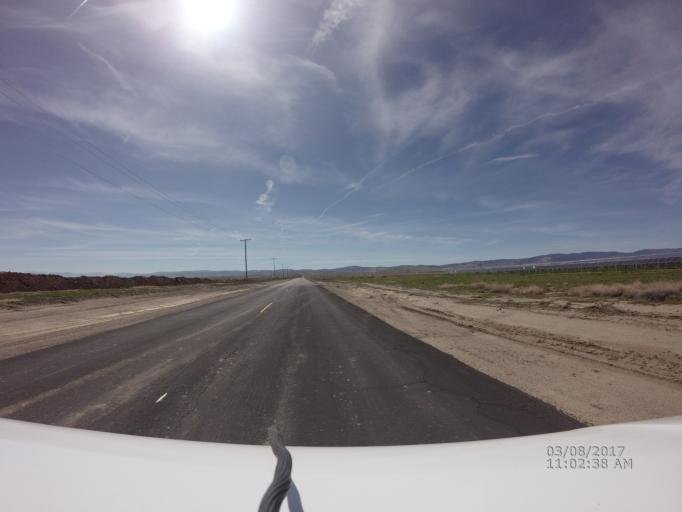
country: US
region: California
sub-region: Los Angeles County
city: Green Valley
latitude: 34.8078
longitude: -118.3791
